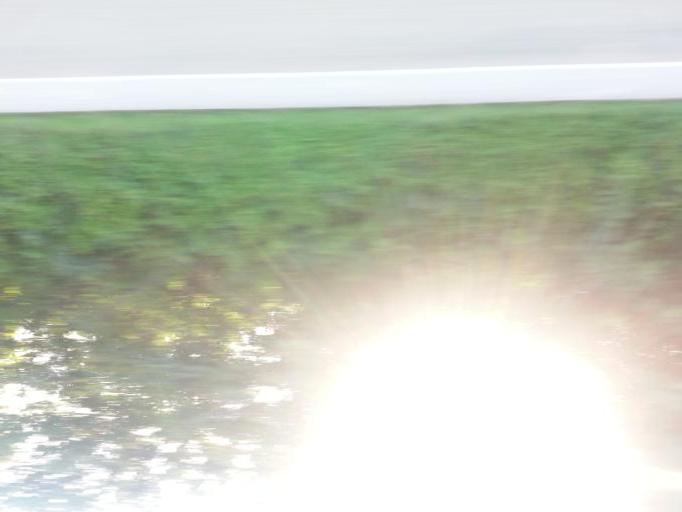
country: US
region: Tennessee
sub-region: Blount County
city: Louisville
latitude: 35.8299
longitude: -84.0173
